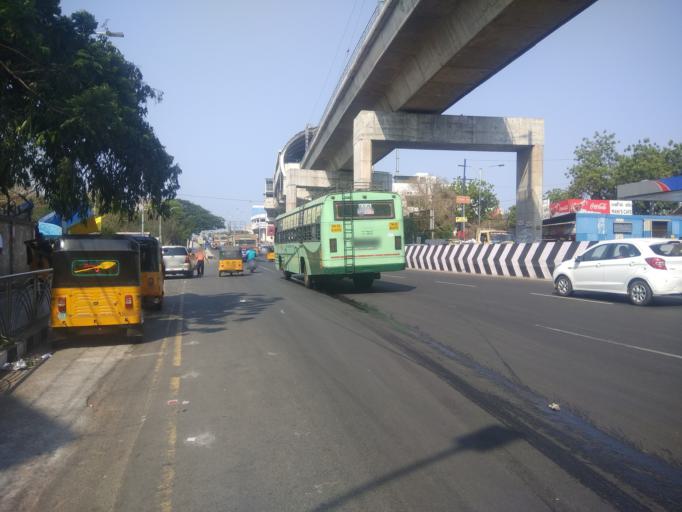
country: IN
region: Tamil Nadu
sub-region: Kancheepuram
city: Alandur
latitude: 13.0091
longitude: 80.2116
